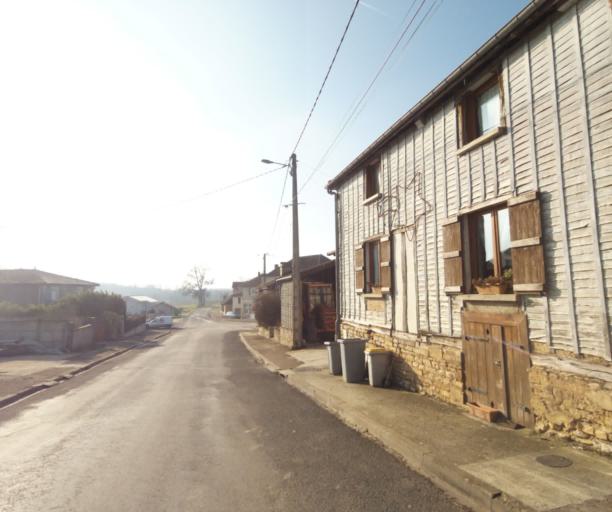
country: FR
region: Champagne-Ardenne
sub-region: Departement de la Haute-Marne
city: Laneuville-a-Remy
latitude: 48.4596
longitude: 4.9161
